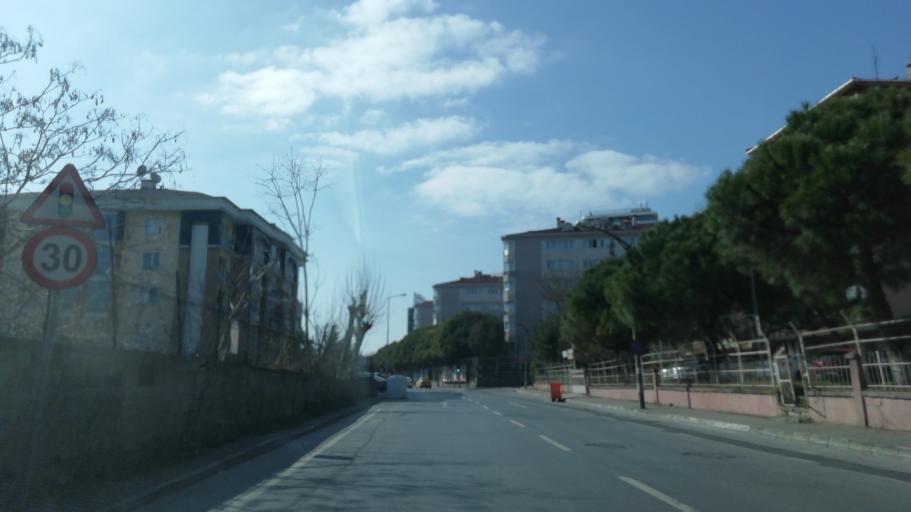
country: TR
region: Istanbul
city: guengoeren merter
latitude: 41.0108
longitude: 28.8961
